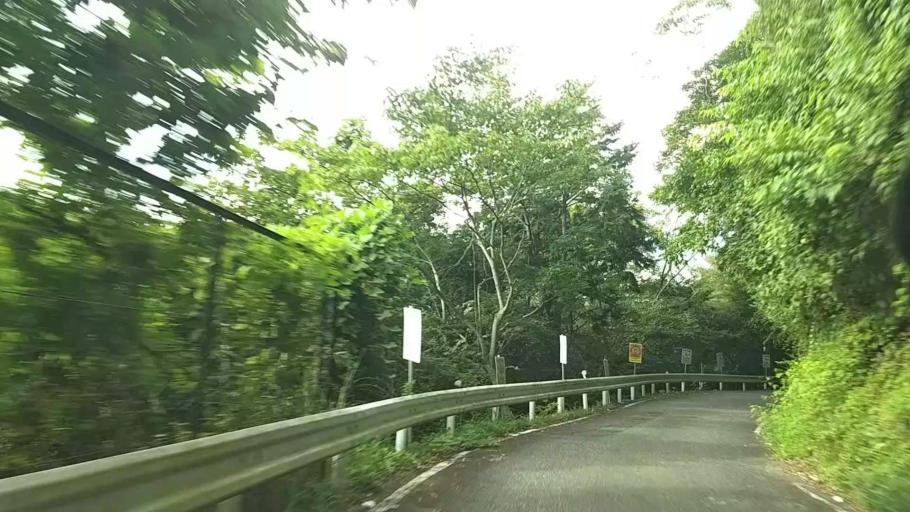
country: JP
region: Shizuoka
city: Fujinomiya
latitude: 35.2178
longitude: 138.5296
